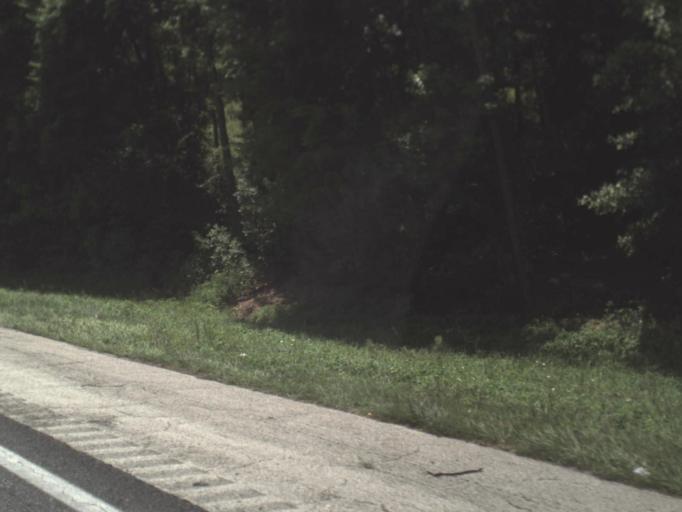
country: US
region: Florida
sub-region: Alachua County
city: Alachua
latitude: 29.7152
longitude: -82.4655
